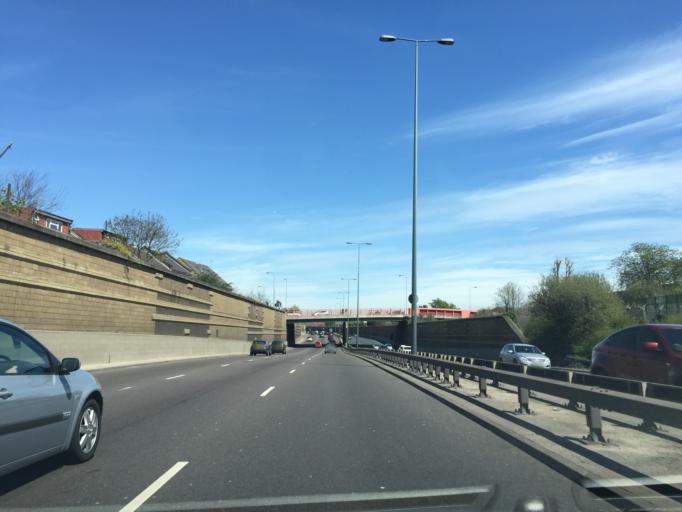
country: GB
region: England
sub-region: Greater London
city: Walthamstow
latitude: 51.5597
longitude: -0.0013
